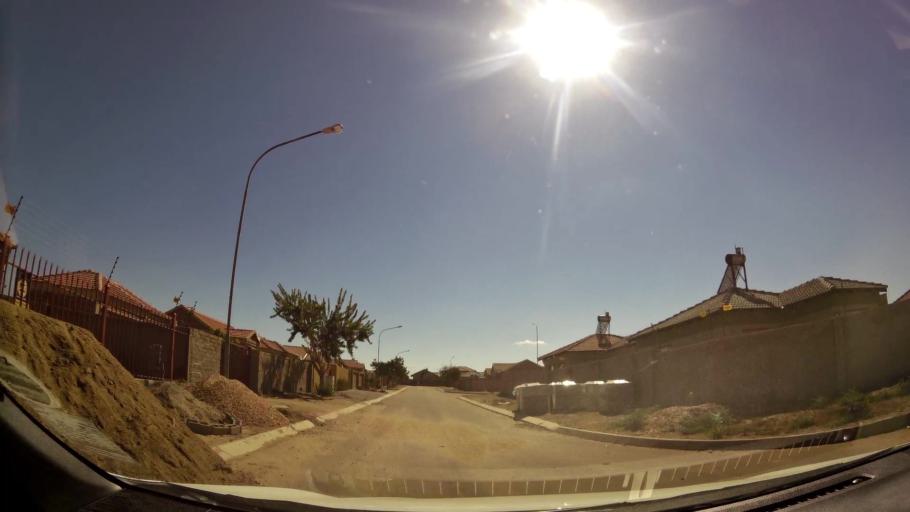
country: ZA
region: Limpopo
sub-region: Capricorn District Municipality
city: Polokwane
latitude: -23.8607
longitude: 29.4245
